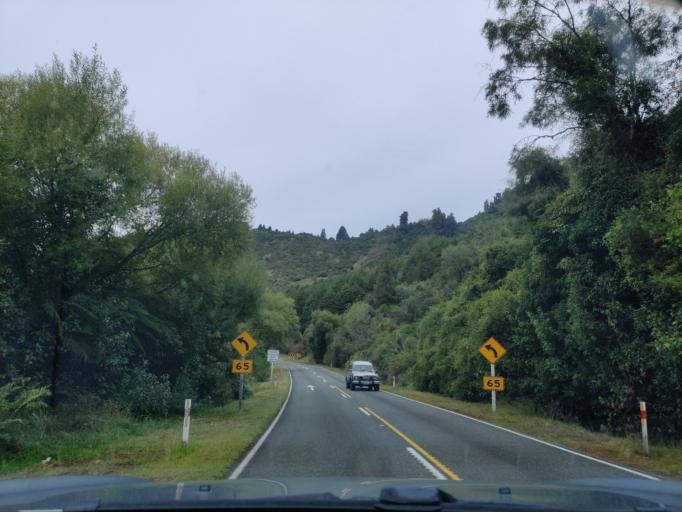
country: NZ
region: West Coast
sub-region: Buller District
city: Westport
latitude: -41.8446
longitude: 171.9115
